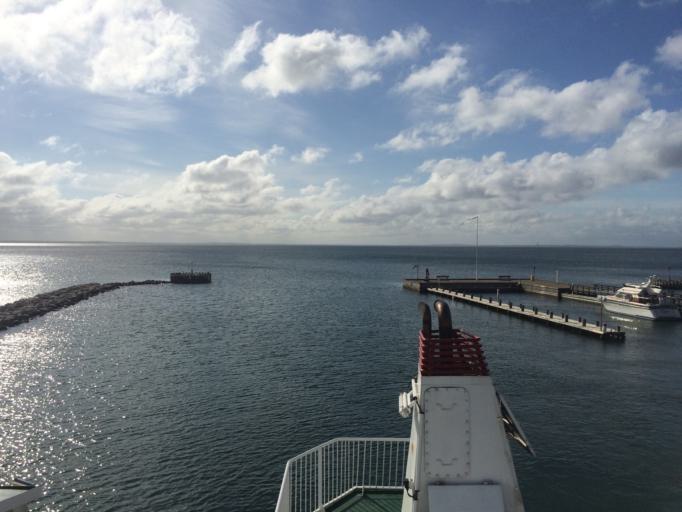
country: DK
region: Zealand
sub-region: Odsherred Kommune
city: Nykobing Sjaelland
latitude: 55.9448
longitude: 11.7680
